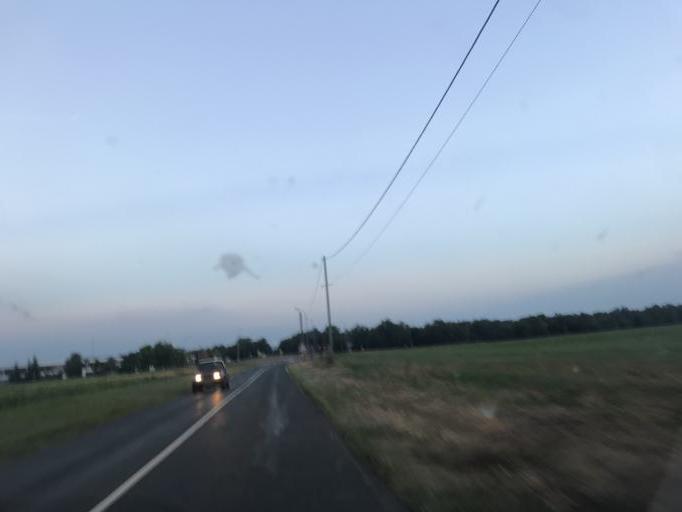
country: FR
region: Rhone-Alpes
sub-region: Departement de l'Ain
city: Chazey-sur-Ain
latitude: 45.8622
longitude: 5.2792
